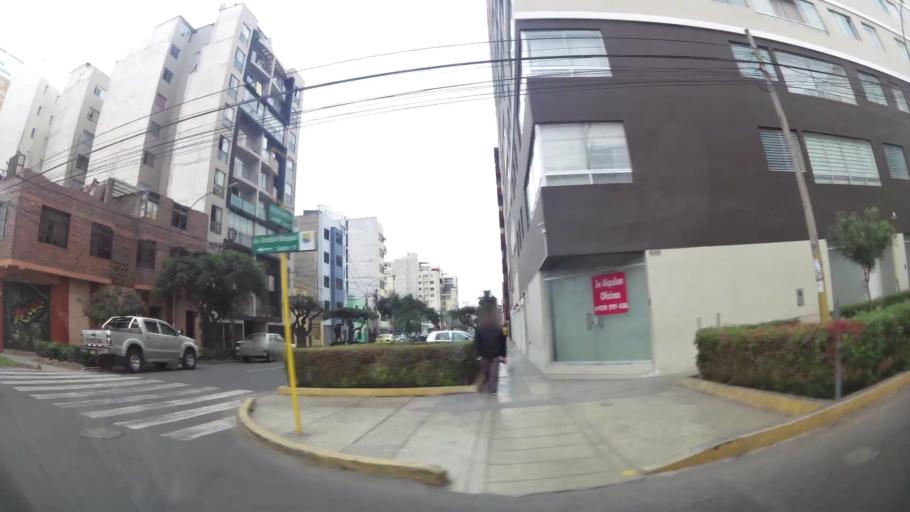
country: PE
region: Lima
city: Lima
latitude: -12.0716
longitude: -77.0478
